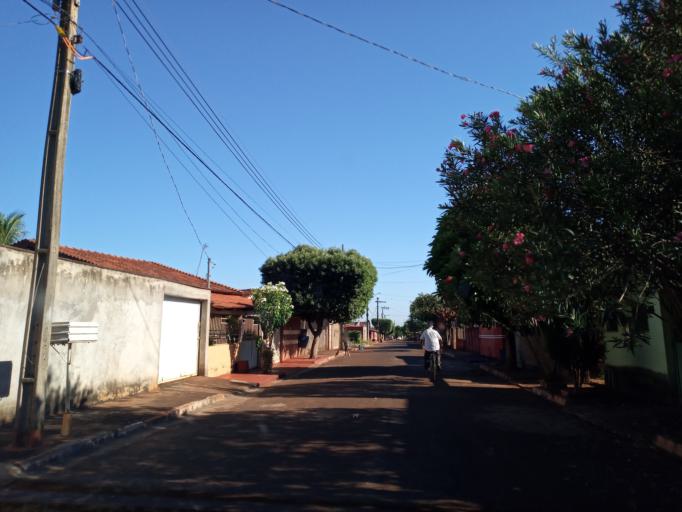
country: BR
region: Minas Gerais
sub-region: Centralina
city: Centralina
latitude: -18.5813
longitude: -49.2053
